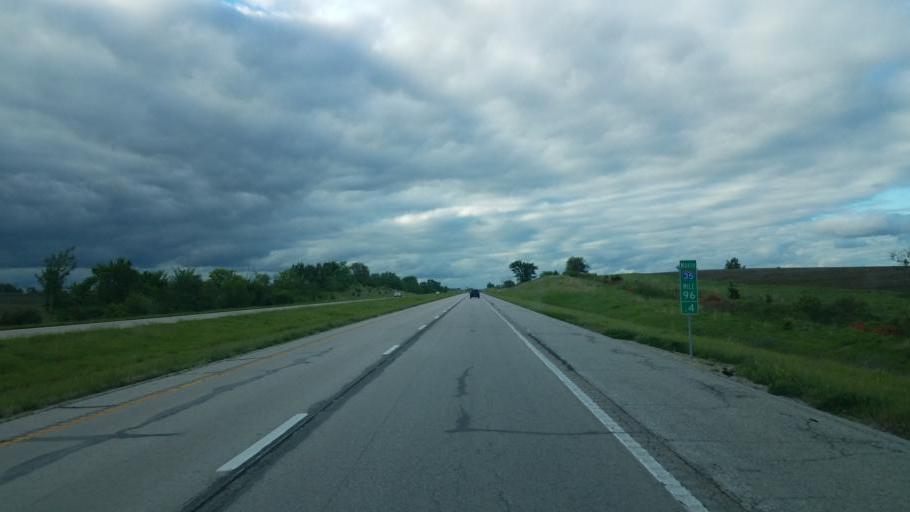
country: US
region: Missouri
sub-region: Harrison County
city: Bethany
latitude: 40.3254
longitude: -94.0114
